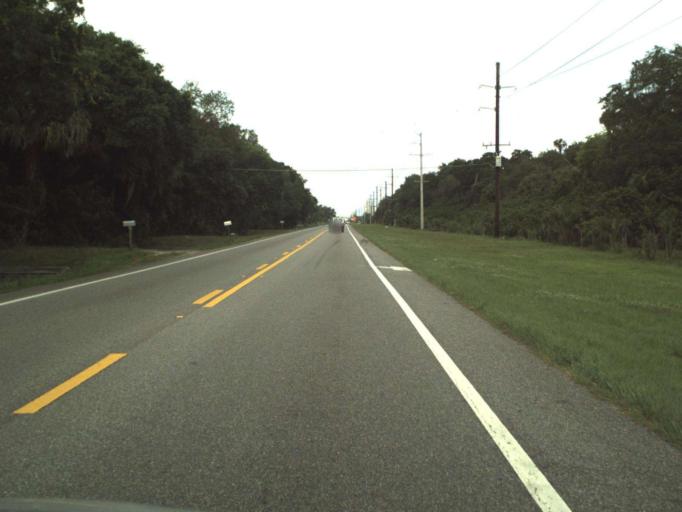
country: US
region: Florida
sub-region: Seminole County
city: Midway
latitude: 28.7869
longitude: -81.2031
